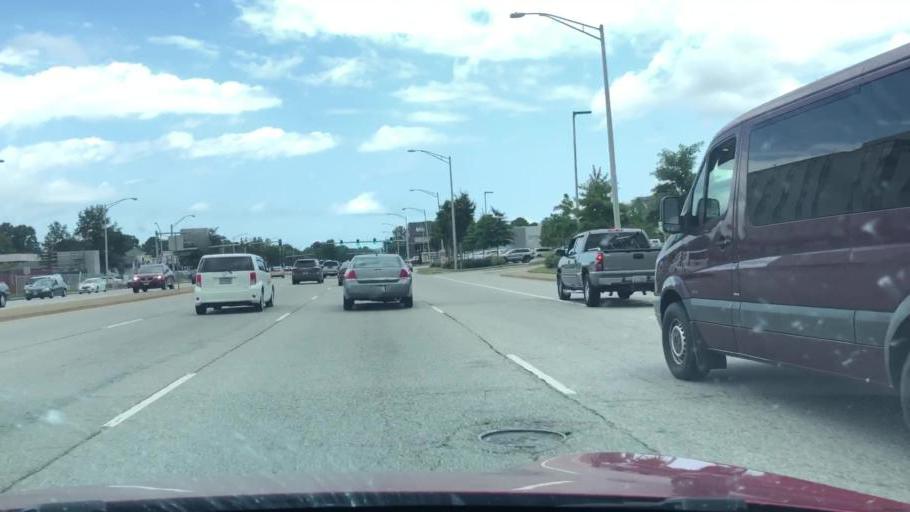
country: US
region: Virginia
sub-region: City of Chesapeake
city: Chesapeake
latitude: 36.8444
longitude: -76.1366
